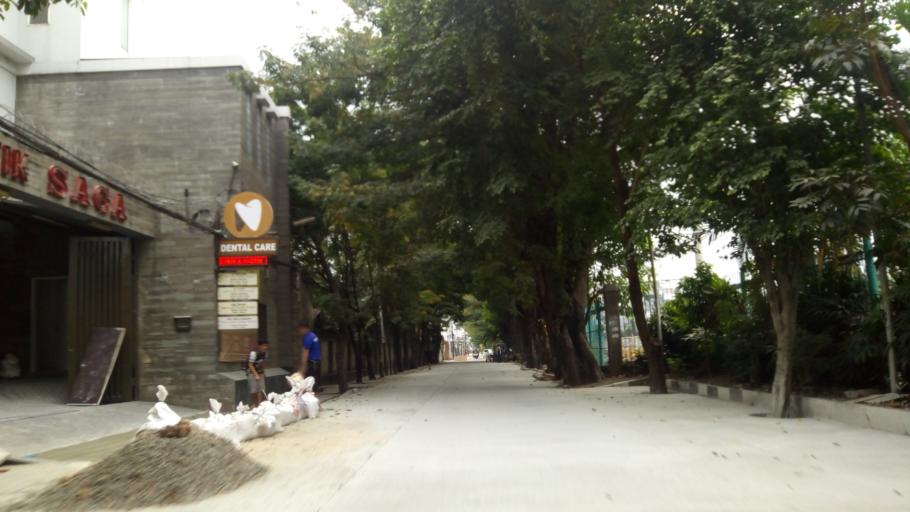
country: ID
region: Jakarta Raya
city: Jakarta
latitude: -6.1578
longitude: 106.8401
